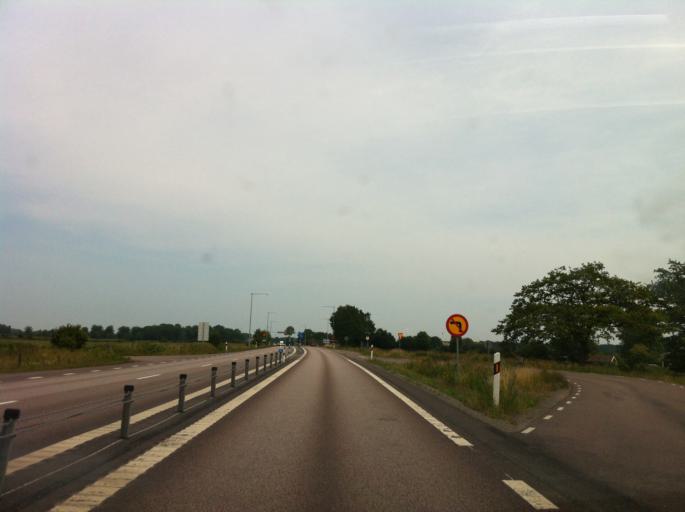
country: SE
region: Kalmar
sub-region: Torsas Kommun
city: Torsas
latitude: 56.3193
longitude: 16.0285
